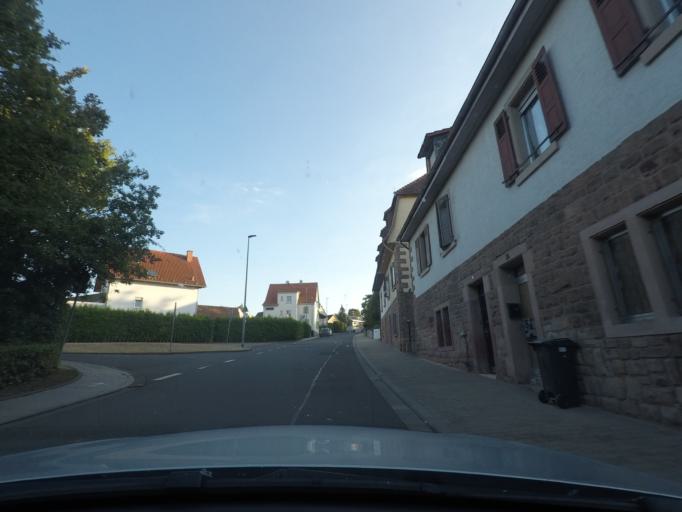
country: DE
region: Rheinland-Pfalz
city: Kirchheimbolanden
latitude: 49.6600
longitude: 8.0105
